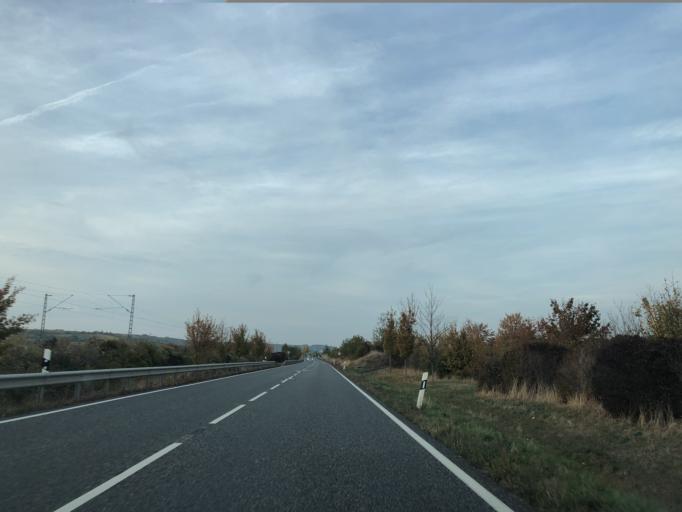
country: DE
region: Rheinland-Pfalz
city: Ludwigshohe
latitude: 49.8124
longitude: 8.3527
